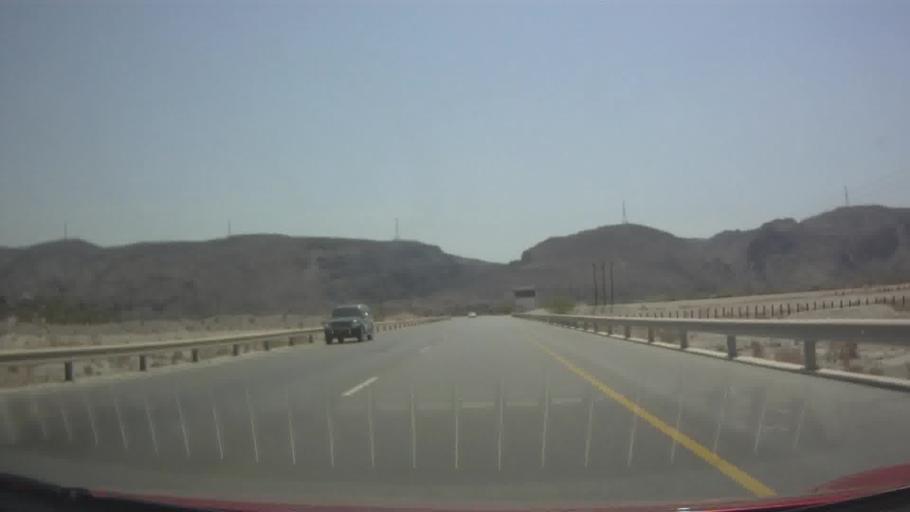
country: OM
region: Muhafazat Masqat
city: Muscat
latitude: 23.5136
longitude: 58.6346
